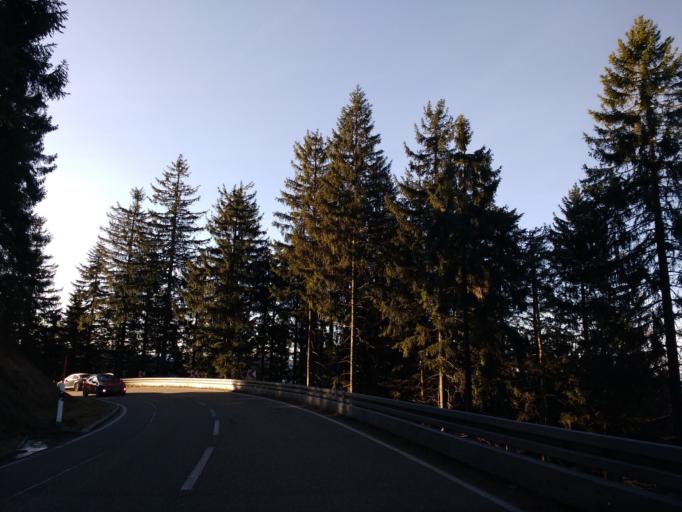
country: DE
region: Baden-Wuerttemberg
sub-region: Freiburg Region
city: Bad Peterstal-Griesbach
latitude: 48.4719
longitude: 8.2639
